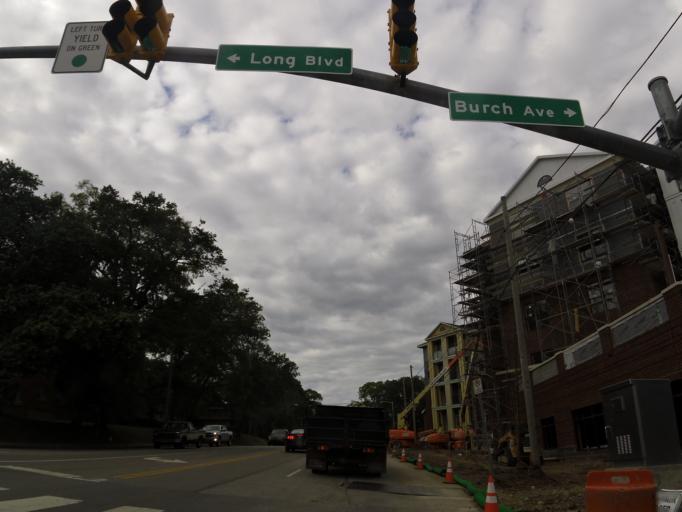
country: US
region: Tennessee
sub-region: Davidson County
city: Nashville
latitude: 36.1464
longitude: -86.8163
